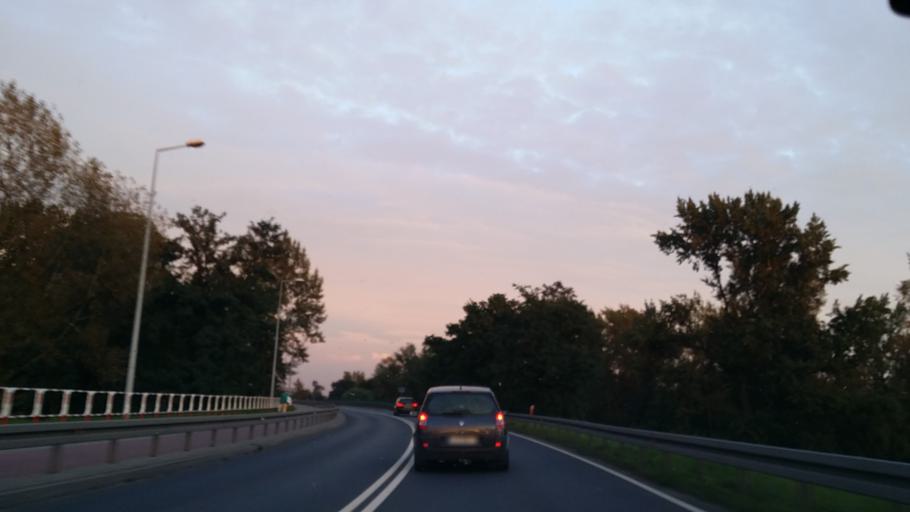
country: PL
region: Lesser Poland Voivodeship
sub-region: Powiat oswiecimski
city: Oswiecim
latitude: 50.0338
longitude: 19.2115
